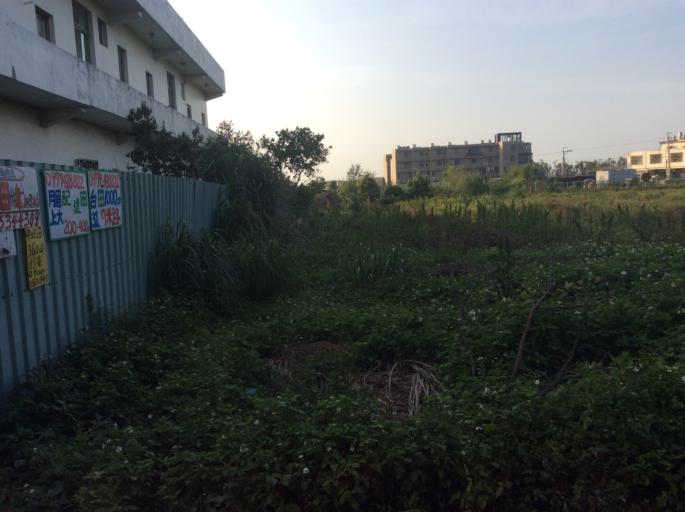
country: TW
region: Taiwan
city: Taoyuan City
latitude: 24.9756
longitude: 121.2054
